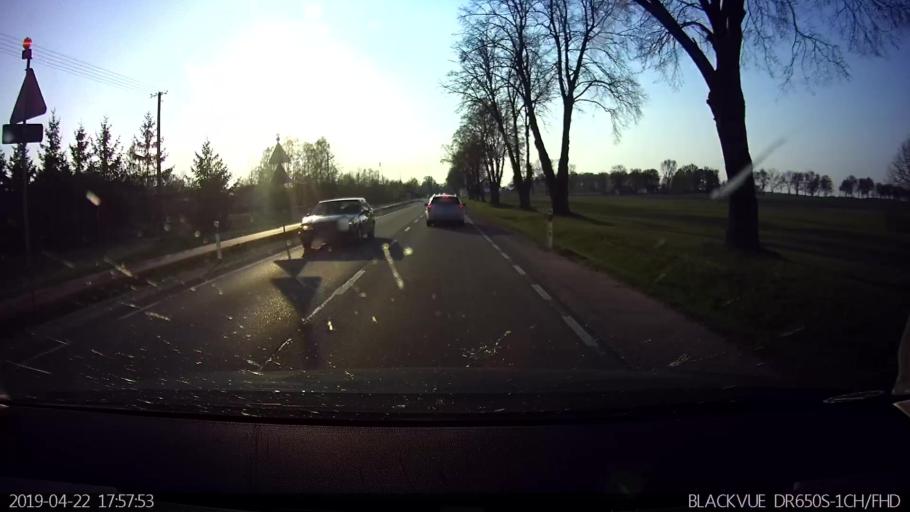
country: PL
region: Masovian Voivodeship
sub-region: Powiat wegrowski
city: Korytnica
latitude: 52.4706
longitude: 21.8842
